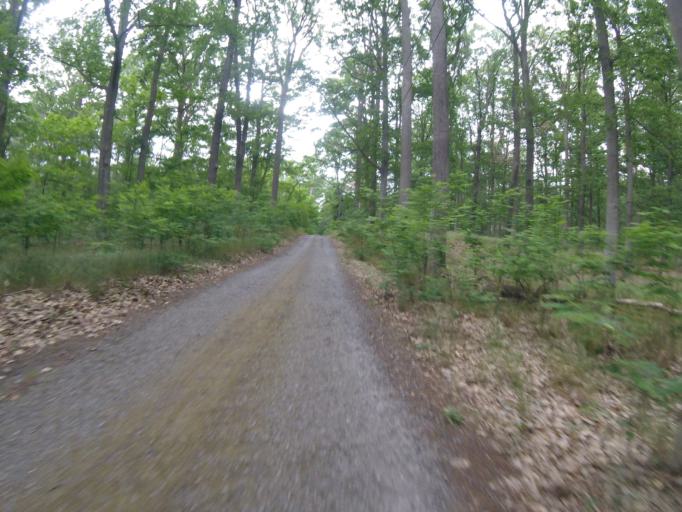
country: DE
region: Brandenburg
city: Gross Koris
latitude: 52.2136
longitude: 13.7032
